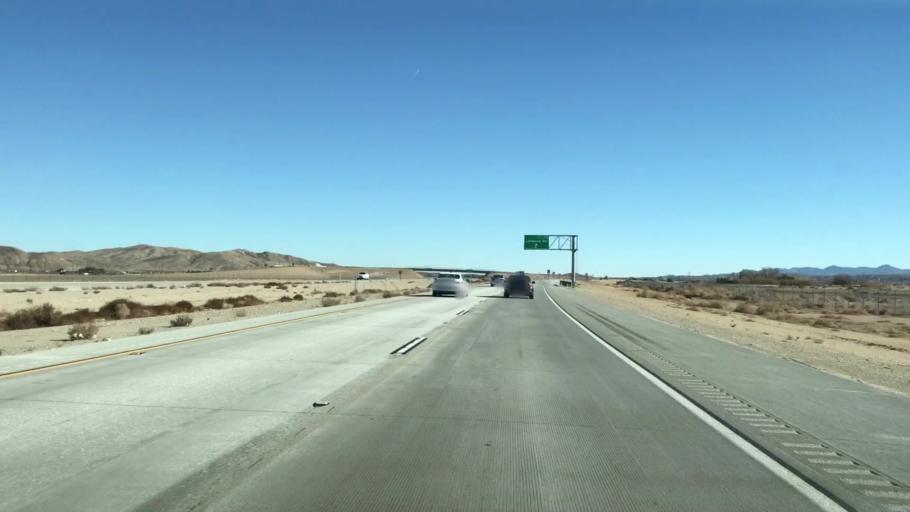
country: US
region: California
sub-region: San Bernardino County
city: Lenwood
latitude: 34.9153
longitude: -117.1281
